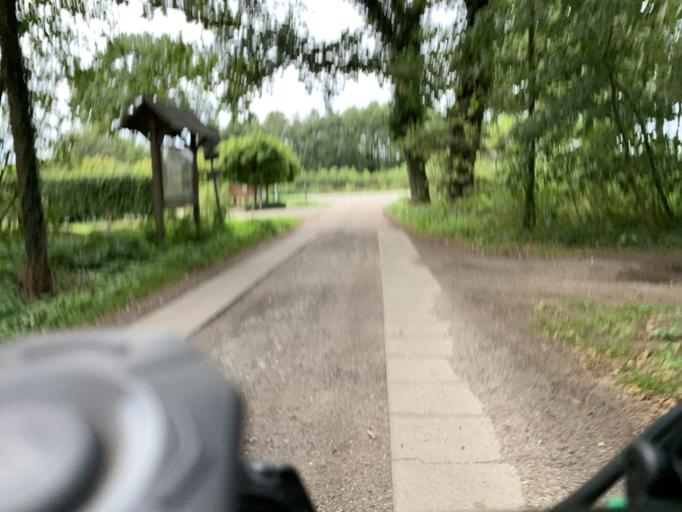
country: DE
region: Lower Saxony
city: Westerstede
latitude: 53.2380
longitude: 7.9144
